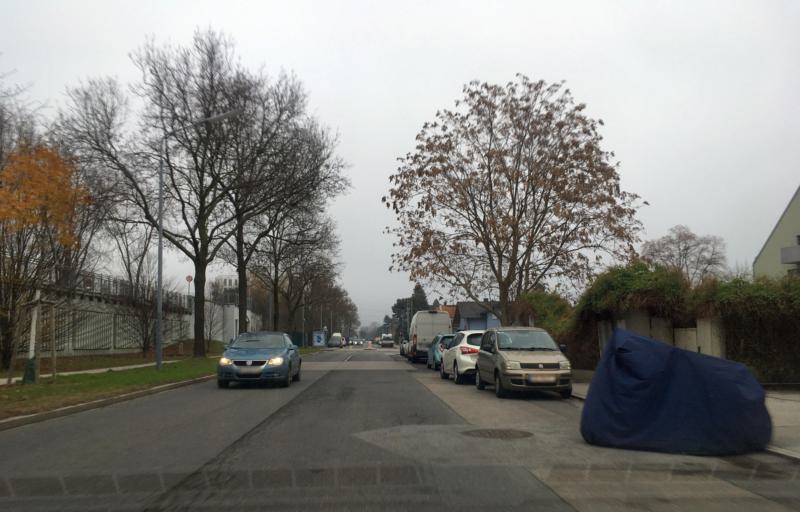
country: AT
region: Lower Austria
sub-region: Politischer Bezirk Wien-Umgebung
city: Gerasdorf bei Wien
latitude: 48.2169
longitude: 16.4641
